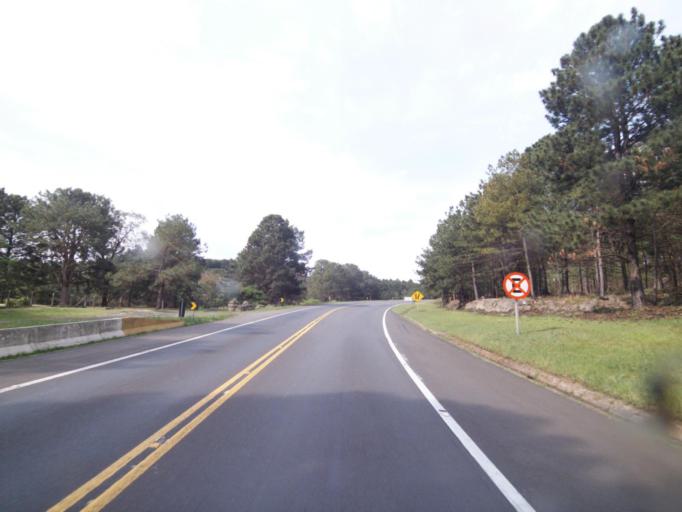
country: BR
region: Parana
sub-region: Campo Largo
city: Campo Largo
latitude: -25.4659
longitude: -49.7665
